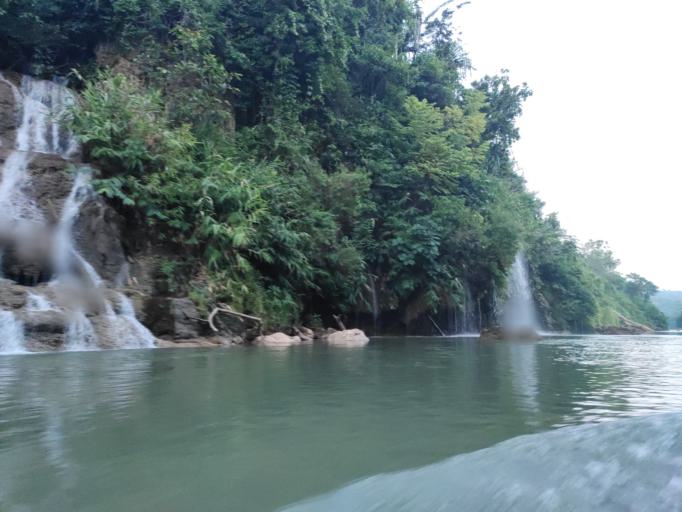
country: MM
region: Mandalay
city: Meiktila
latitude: 21.0137
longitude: 96.3933
